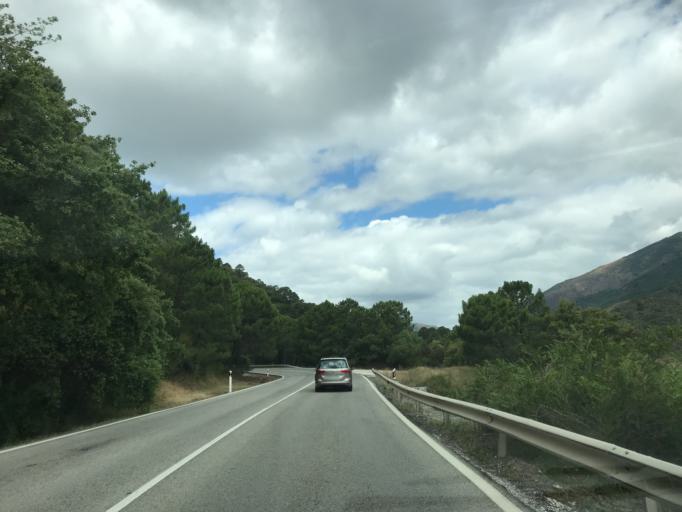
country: ES
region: Andalusia
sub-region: Provincia de Malaga
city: Benahavis
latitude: 36.5414
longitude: -5.0159
